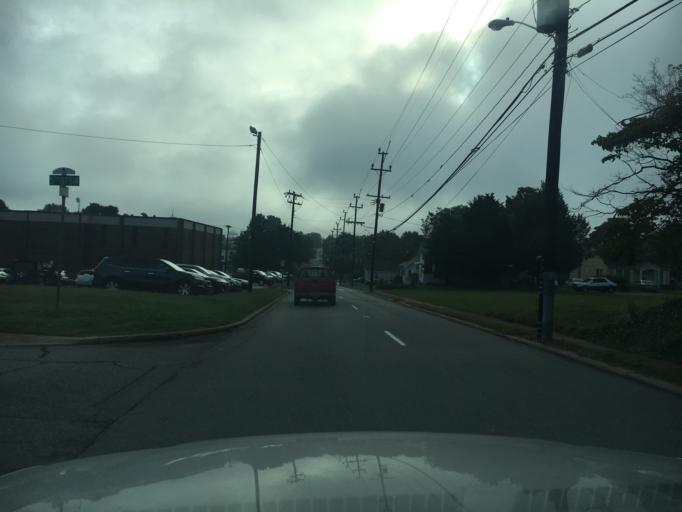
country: US
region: North Carolina
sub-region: Catawba County
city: Hickory
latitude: 35.7300
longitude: -81.3463
